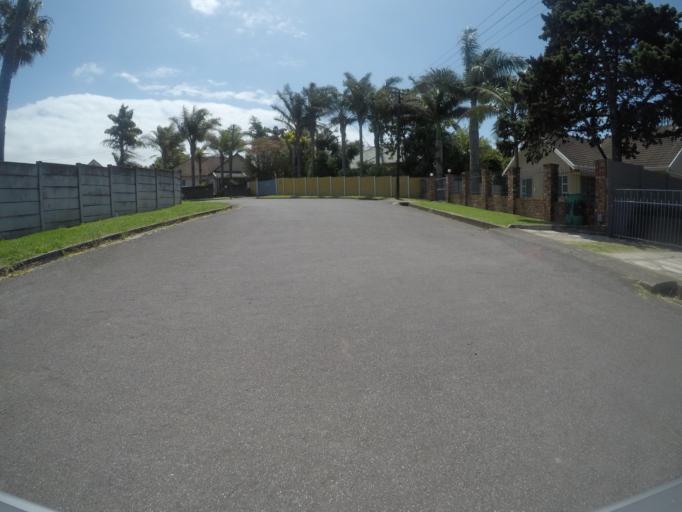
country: ZA
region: Eastern Cape
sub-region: Buffalo City Metropolitan Municipality
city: East London
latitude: -32.9713
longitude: 27.8678
